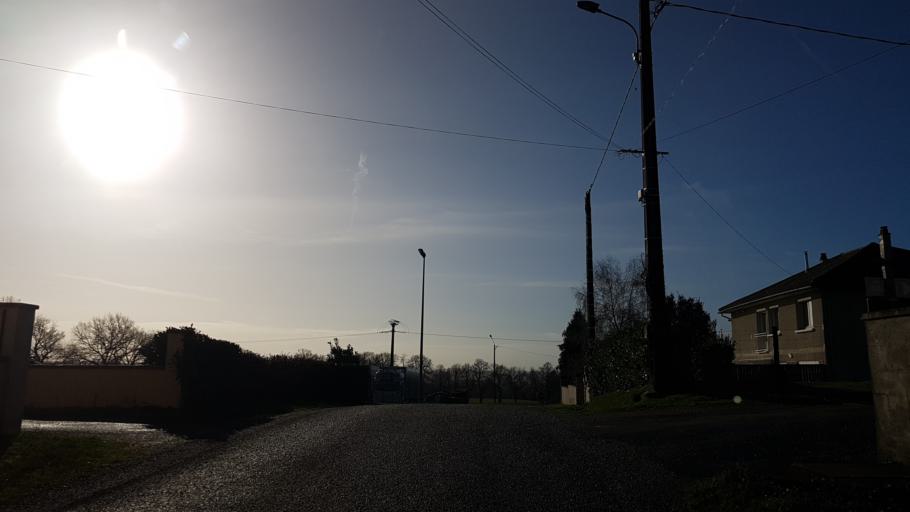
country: FR
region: Poitou-Charentes
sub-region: Departement de la Charente
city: Etagnac
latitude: 45.8949
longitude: 0.8007
